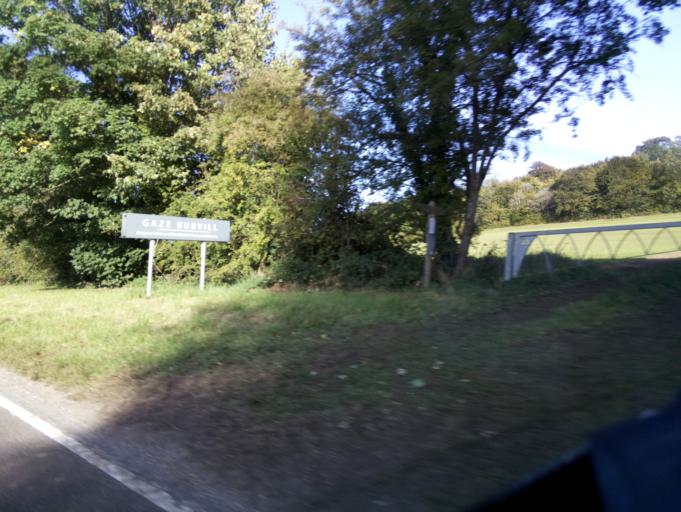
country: GB
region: England
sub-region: Hampshire
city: Four Marks
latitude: 51.0939
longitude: -0.9966
